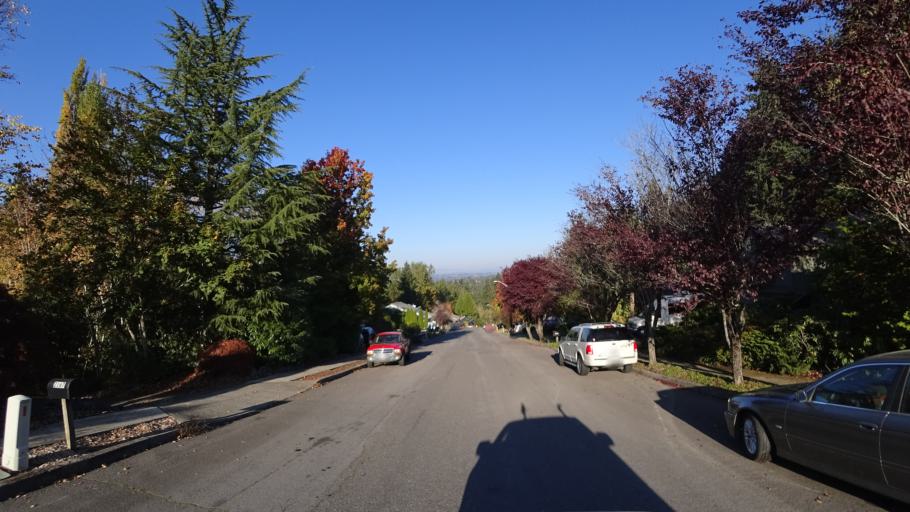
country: US
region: Oregon
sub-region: Multnomah County
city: Gresham
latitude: 45.4811
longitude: -122.4302
